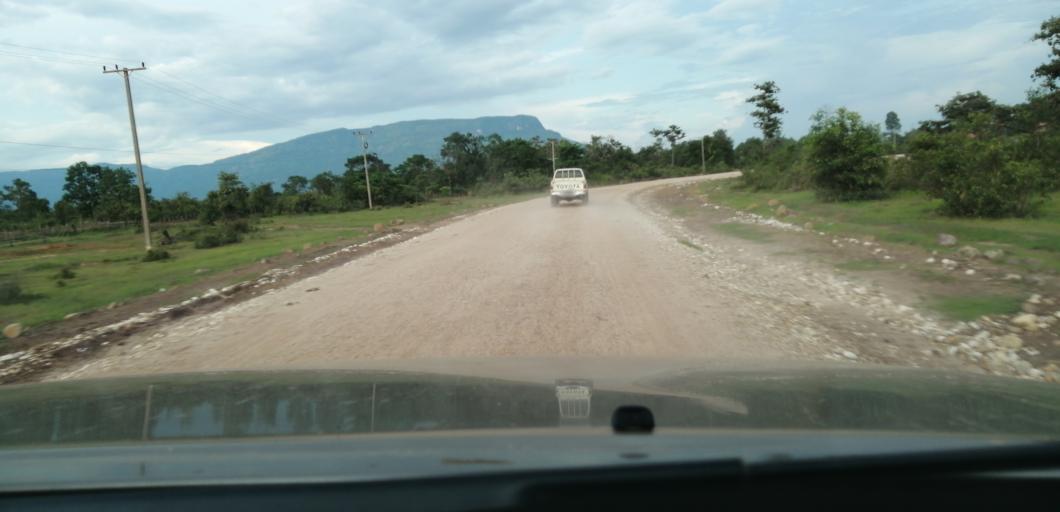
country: LA
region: Attapu
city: Attapu
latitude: 14.7101
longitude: 106.4887
